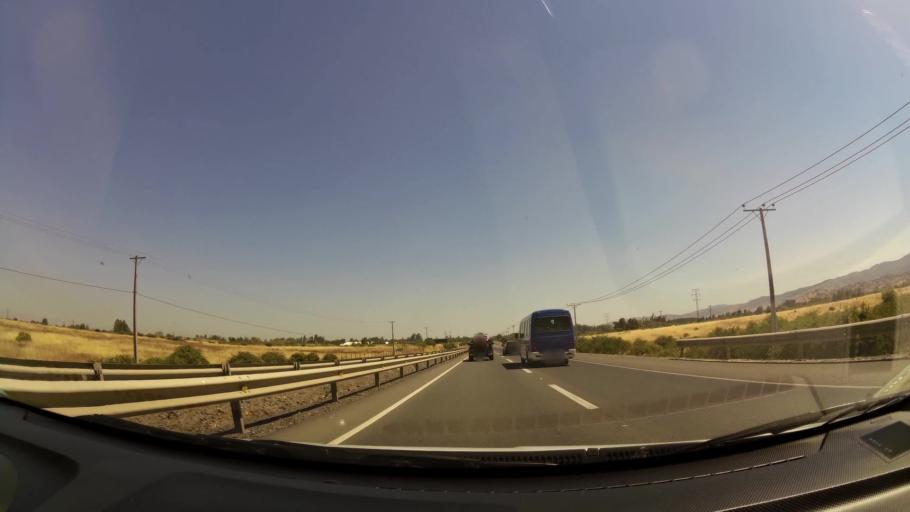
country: CL
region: Maule
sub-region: Provincia de Talca
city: Talca
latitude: -35.3250
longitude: -71.5458
